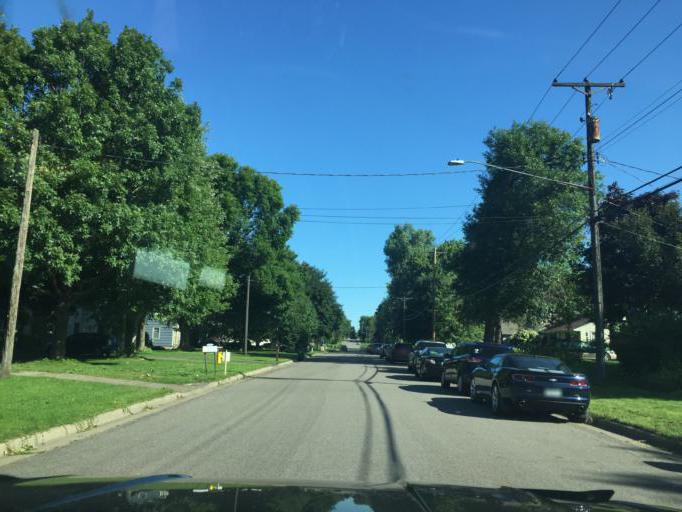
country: US
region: Minnesota
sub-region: Ramsey County
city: Roseville
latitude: 44.9934
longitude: -93.1414
